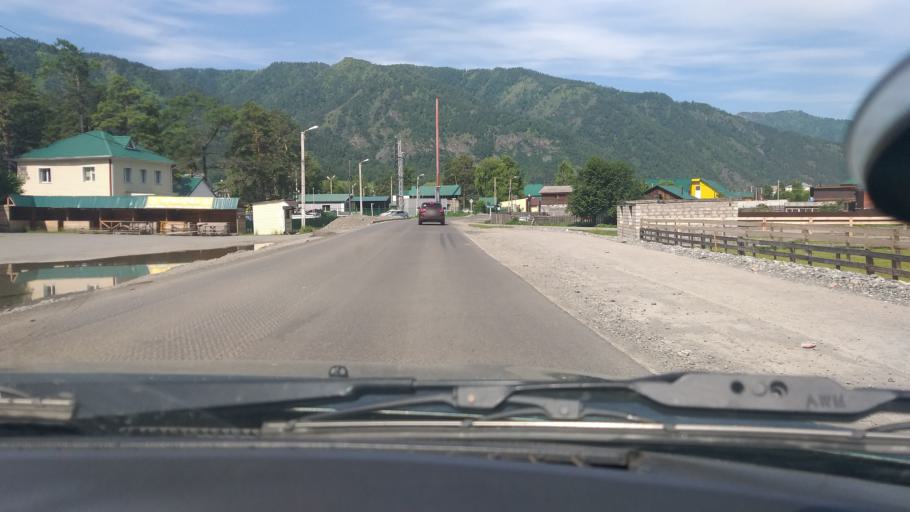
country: RU
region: Altay
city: Chemal
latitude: 51.4037
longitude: 86.0111
